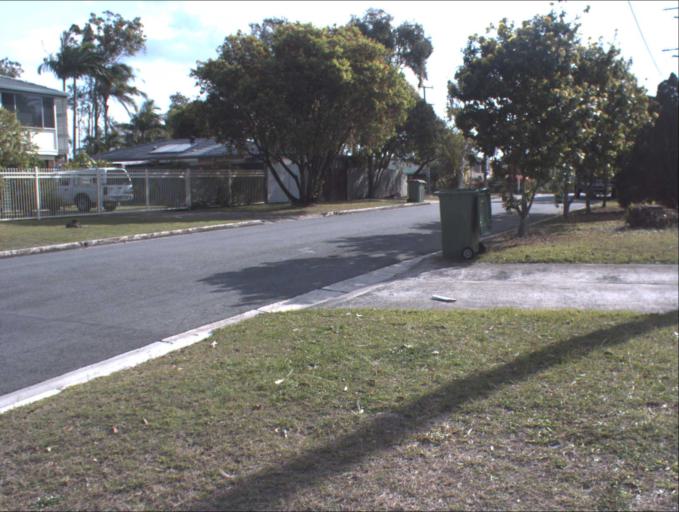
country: AU
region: Queensland
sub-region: Logan
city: Waterford West
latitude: -27.6700
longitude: 153.1246
